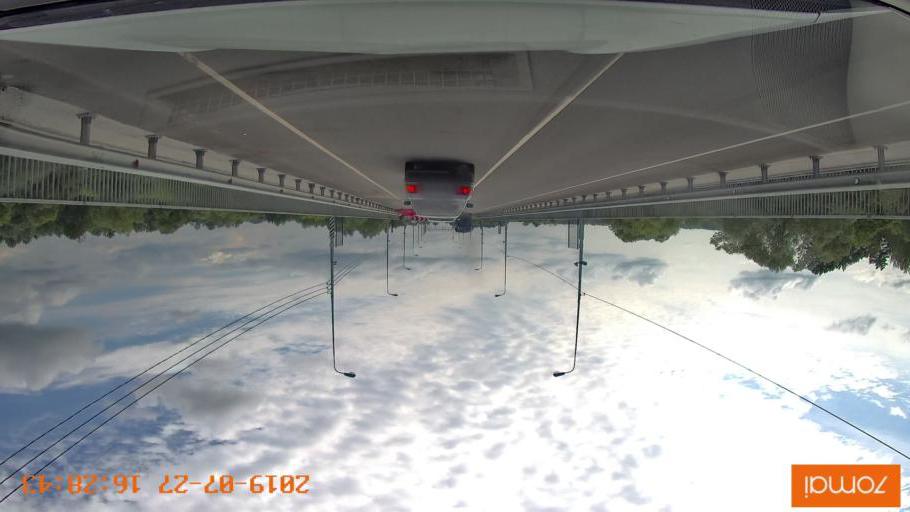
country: RU
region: Kaliningrad
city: Gvardeysk
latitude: 54.6484
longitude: 21.3565
